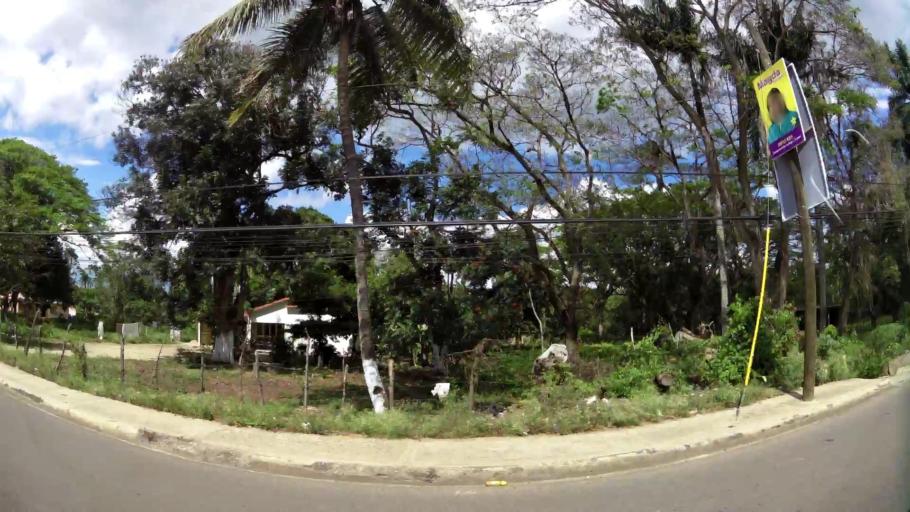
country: DO
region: Santiago
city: Santiago de los Caballeros
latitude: 19.4044
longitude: -70.6609
